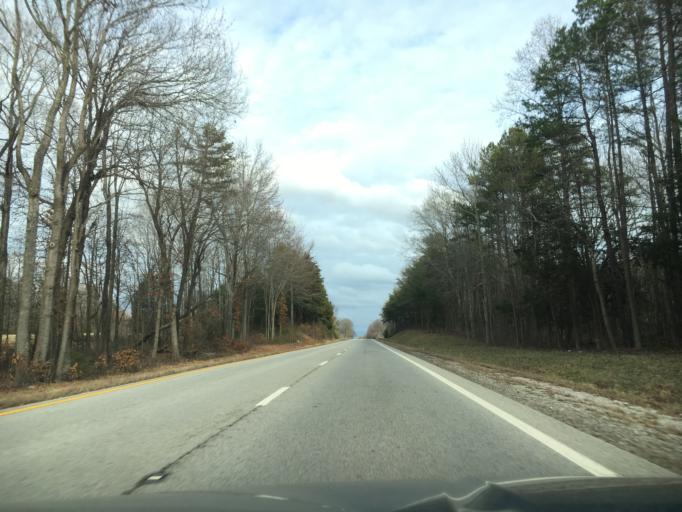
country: US
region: Virginia
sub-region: Lunenburg County
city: Victoria
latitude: 37.1412
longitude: -78.3042
